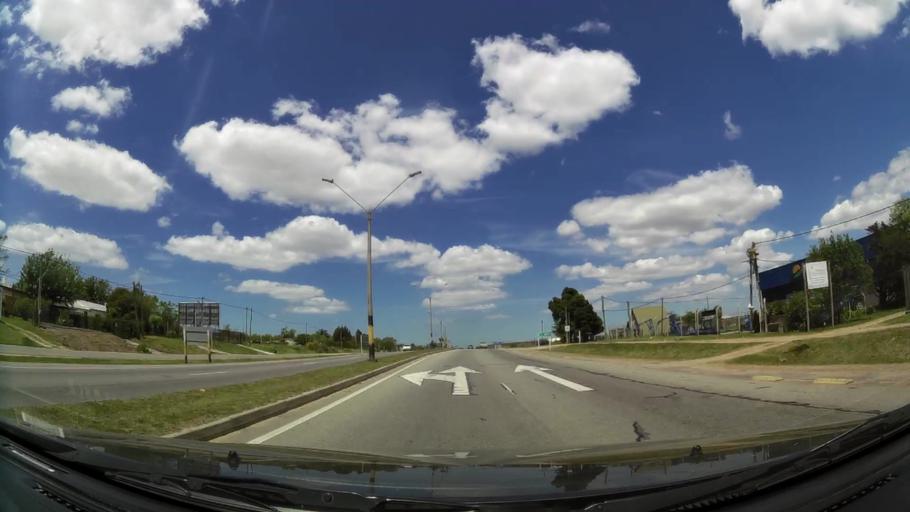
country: UY
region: Canelones
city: Colonia Nicolich
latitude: -34.8227
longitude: -56.0091
